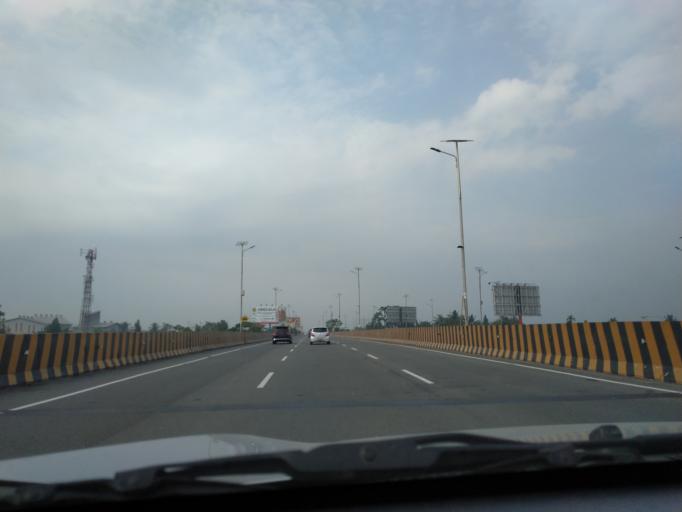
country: ID
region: North Sumatra
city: Percut
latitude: 3.6097
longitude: 98.8537
